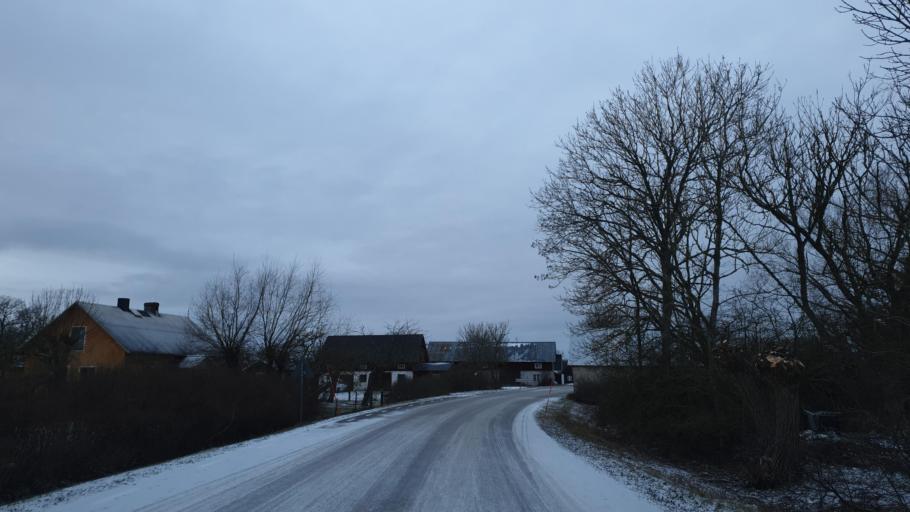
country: SE
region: Gotland
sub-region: Gotland
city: Slite
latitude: 57.4220
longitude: 18.9068
